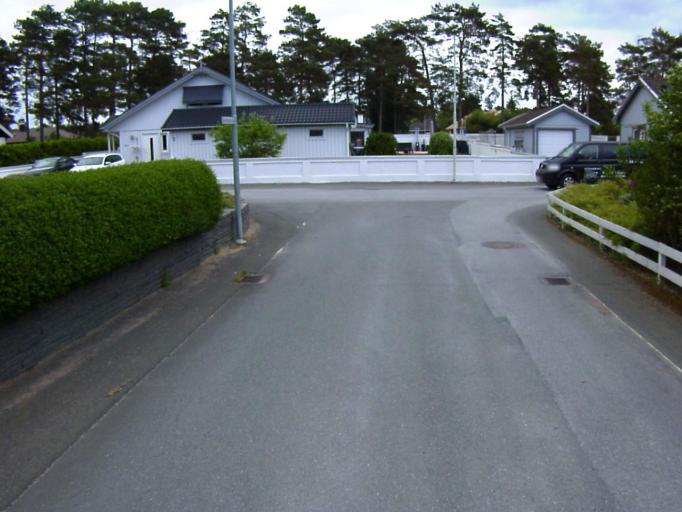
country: SE
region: Skane
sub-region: Kristianstads Kommun
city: Ahus
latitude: 55.9391
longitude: 14.2750
